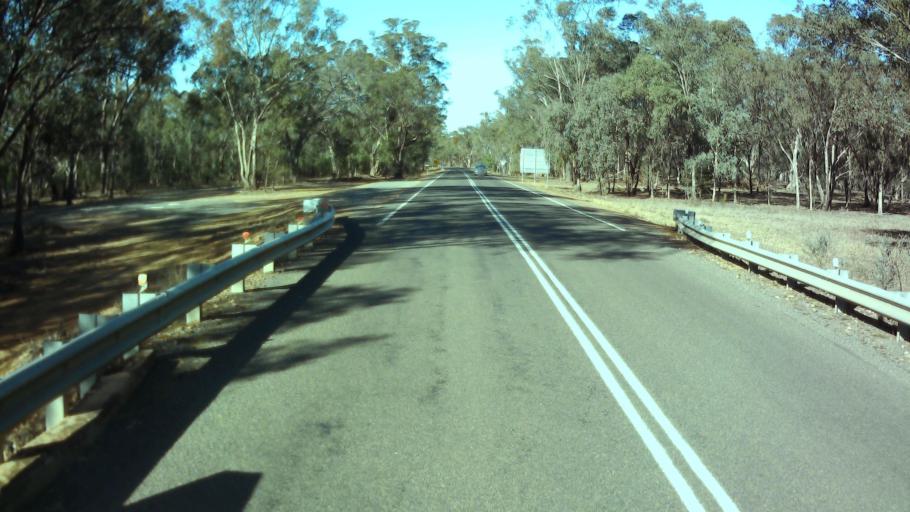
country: AU
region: New South Wales
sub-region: Weddin
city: Grenfell
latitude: -34.0010
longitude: 148.1295
